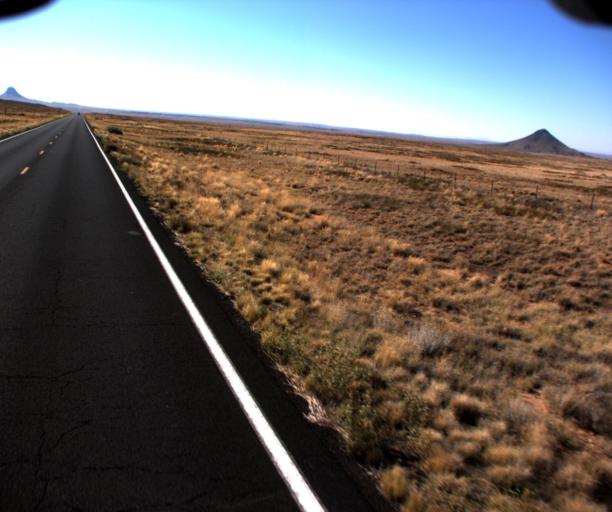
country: US
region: Arizona
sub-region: Navajo County
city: Dilkon
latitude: 35.4051
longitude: -110.4264
